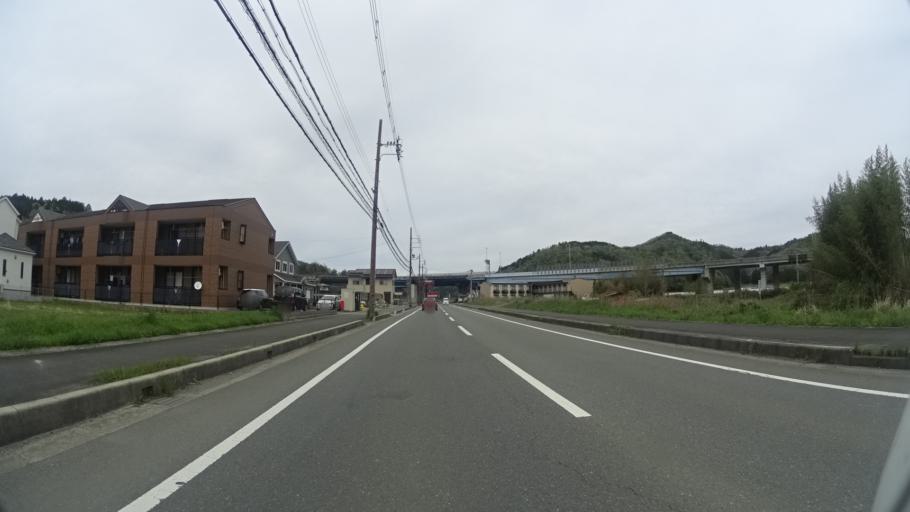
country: JP
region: Kyoto
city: Kameoka
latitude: 35.1197
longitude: 135.4786
